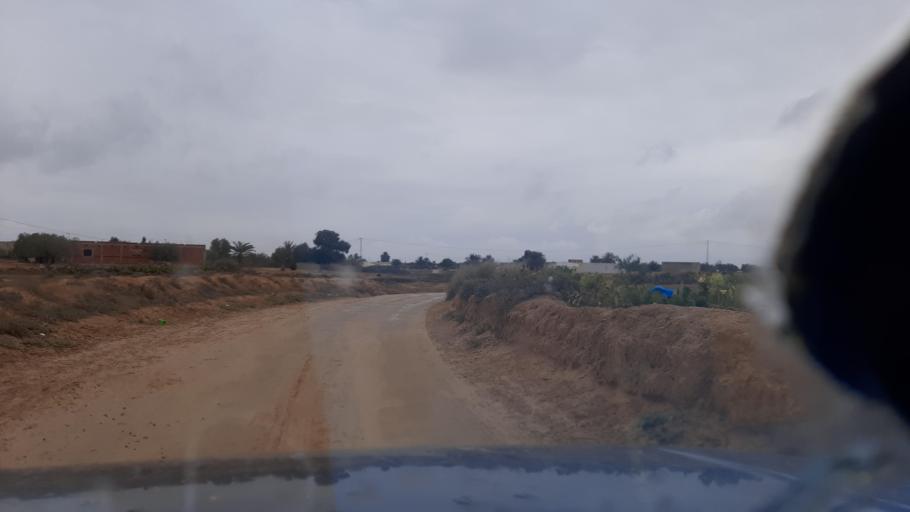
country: TN
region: Al Mahdiyah
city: Shurban
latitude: 35.4357
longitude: 10.4024
